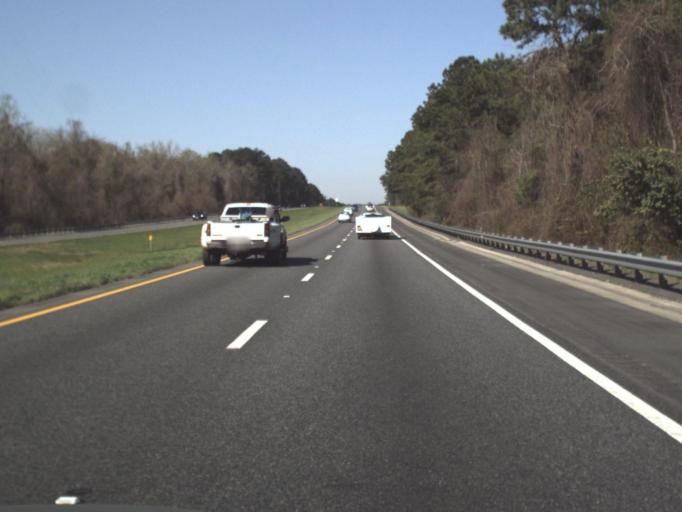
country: US
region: Florida
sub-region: Leon County
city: Tallahassee
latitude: 30.4985
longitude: -84.1957
